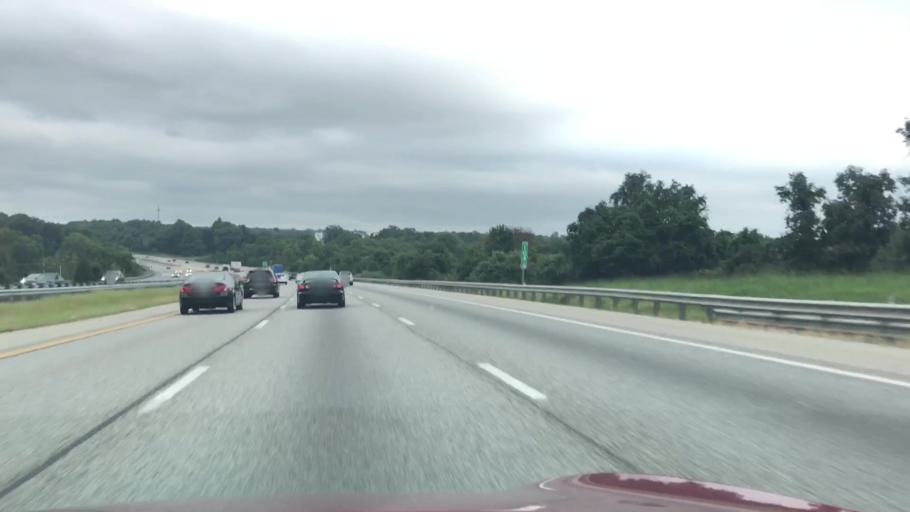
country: US
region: Maryland
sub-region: Cecil County
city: Elkton
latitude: 39.6427
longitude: -75.8719
